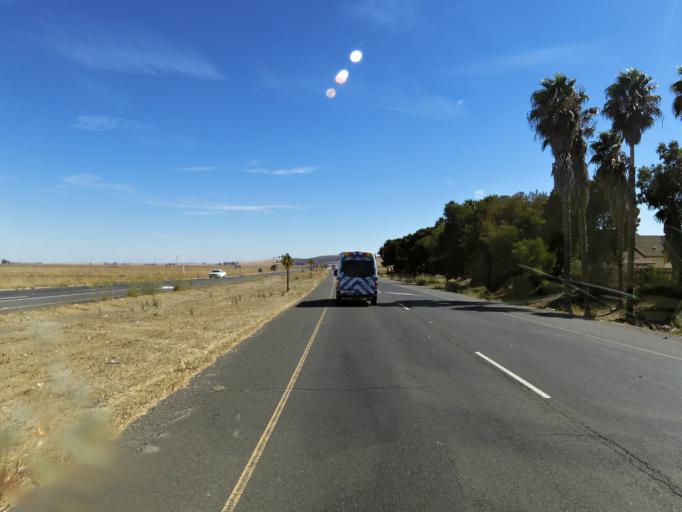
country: US
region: California
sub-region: Solano County
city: Suisun
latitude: 38.2400
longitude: -121.9897
